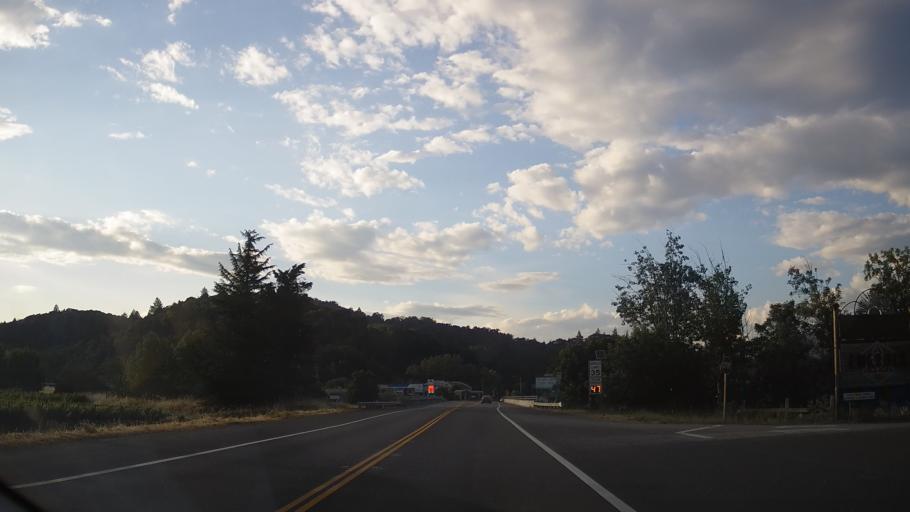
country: US
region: California
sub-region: Mendocino County
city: Talmage
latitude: 38.9674
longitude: -123.1156
